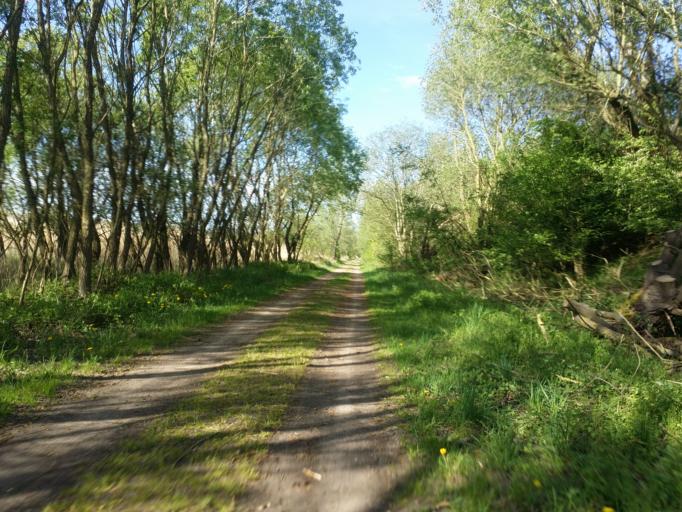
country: DE
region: Lower Saxony
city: Lemwerder
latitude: 53.1429
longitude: 8.6647
